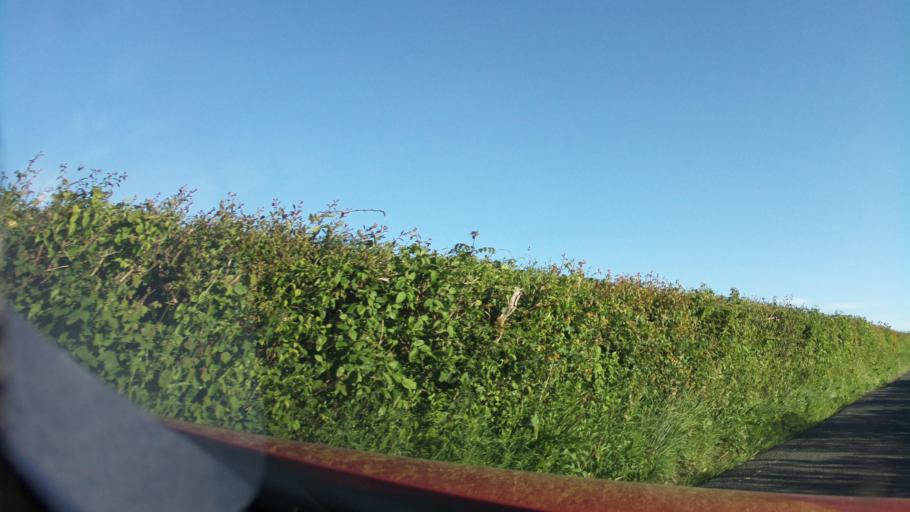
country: GB
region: England
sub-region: Devon
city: Axminster
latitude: 50.7362
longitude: -2.9889
